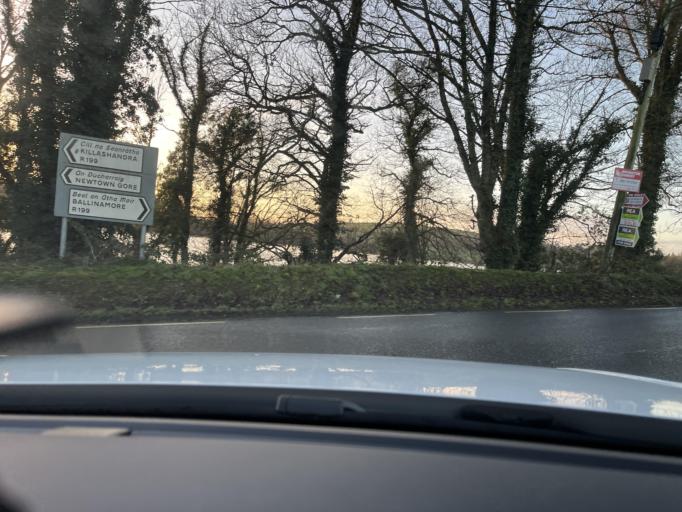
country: IE
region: Ulster
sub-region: An Cabhan
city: Ballyconnell
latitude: 54.0594
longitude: -7.6925
